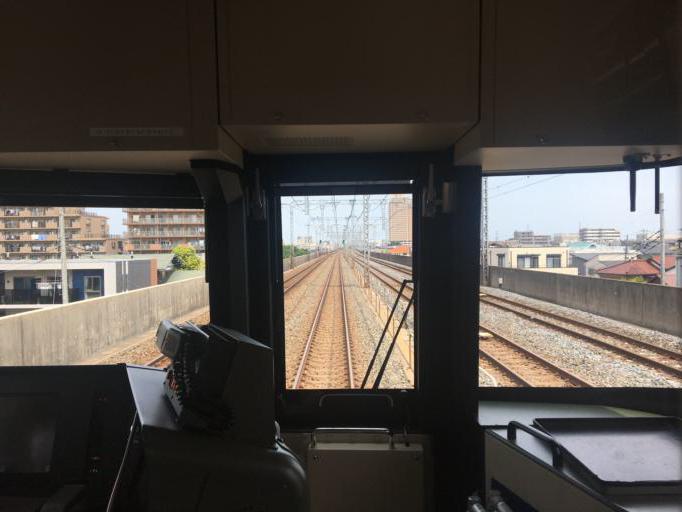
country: JP
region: Saitama
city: Koshigaya
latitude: 35.8935
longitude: 139.7835
